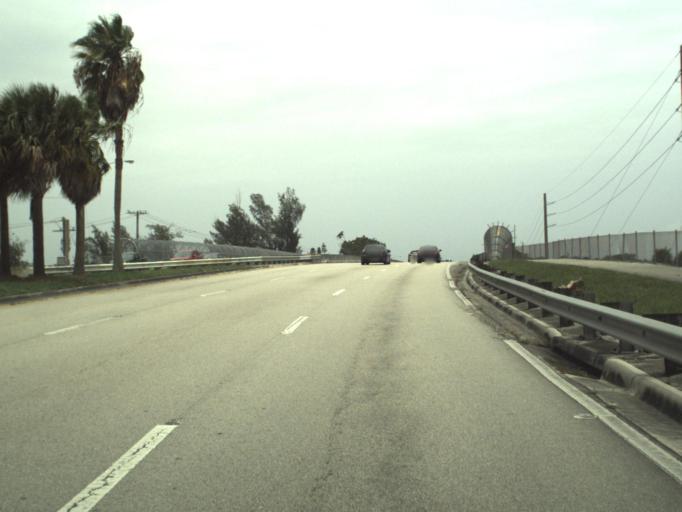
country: US
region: Florida
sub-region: Palm Beach County
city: Boca Pointe
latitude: 26.3501
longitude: -80.1724
